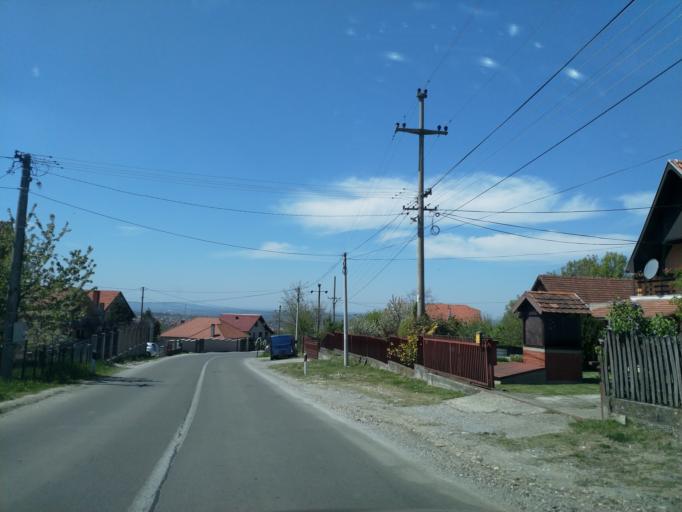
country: RS
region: Central Serbia
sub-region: Belgrade
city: Lazarevac
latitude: 44.3721
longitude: 20.3019
